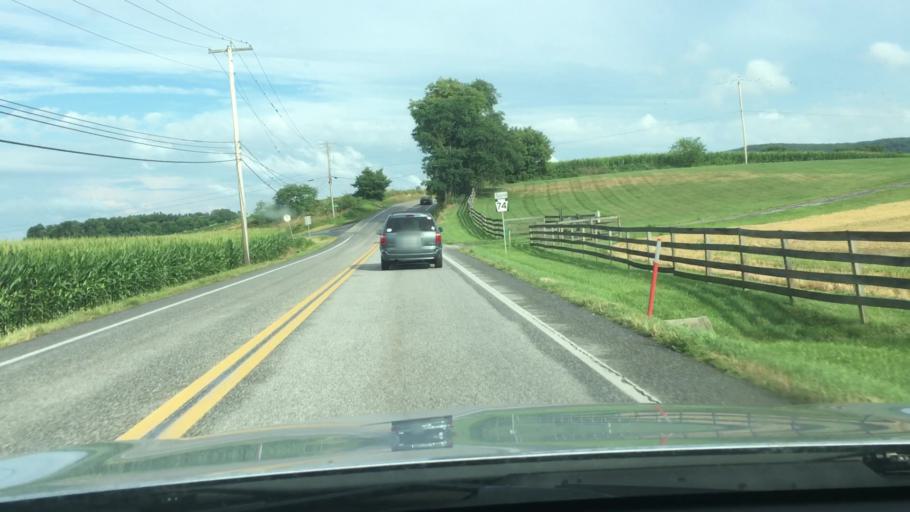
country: US
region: Pennsylvania
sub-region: Cumberland County
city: Boiling Springs
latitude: 40.1536
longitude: -77.0796
